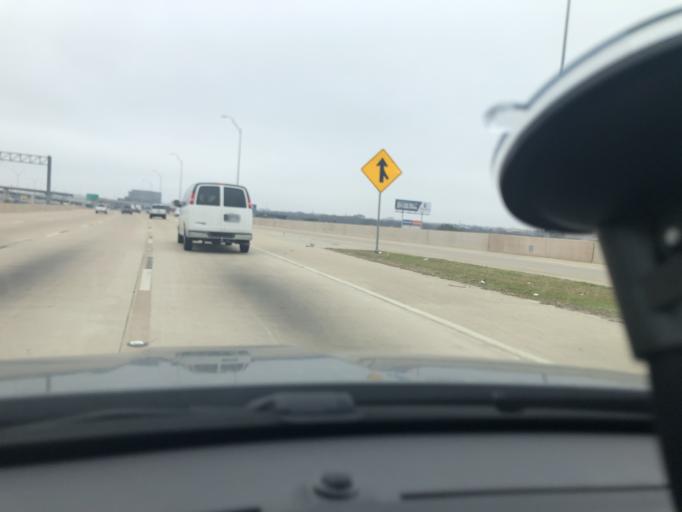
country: US
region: Texas
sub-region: Tarrant County
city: Fort Worth
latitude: 32.7387
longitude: -97.3517
